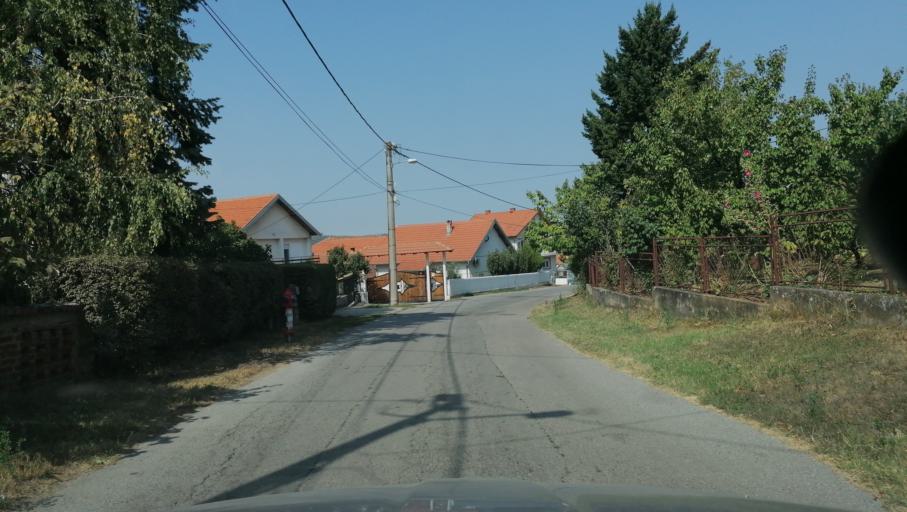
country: RS
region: Central Serbia
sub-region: Belgrade
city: Zvezdara
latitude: 44.6984
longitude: 20.5503
